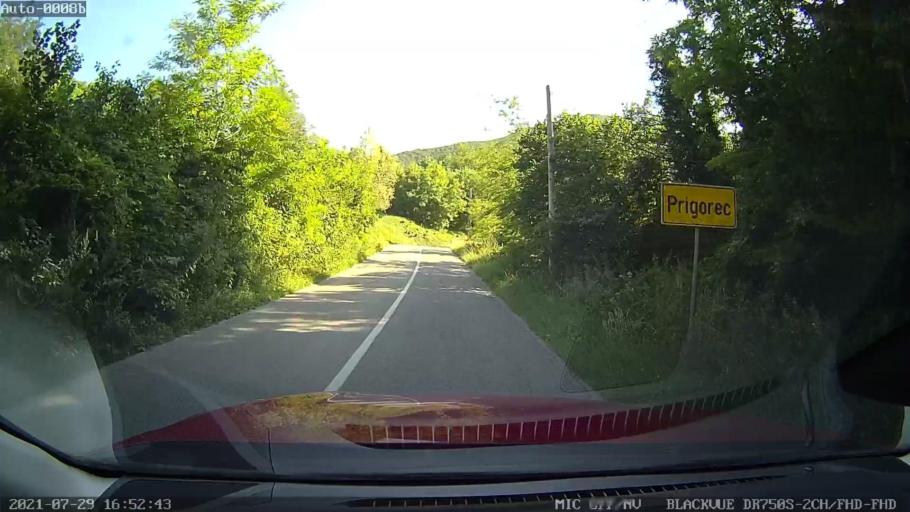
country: HR
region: Varazdinska
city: Ivanec
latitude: 46.2019
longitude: 16.1347
